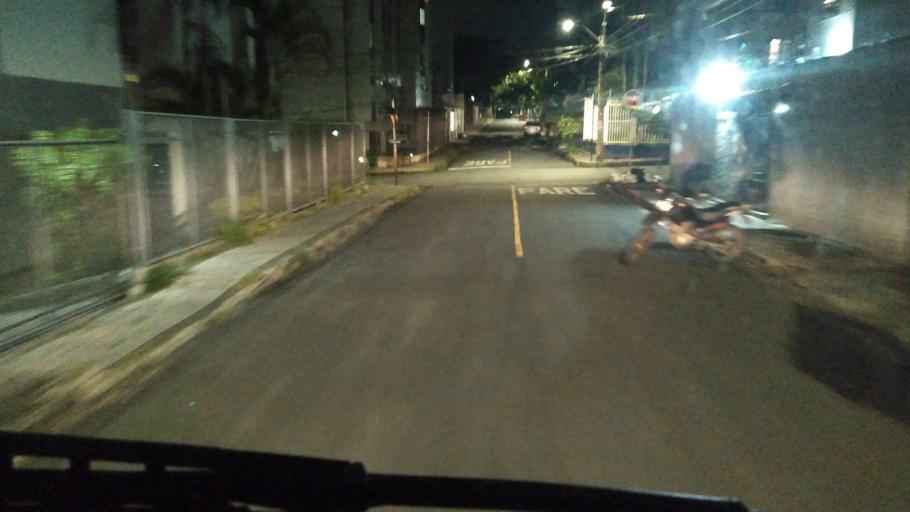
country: BR
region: Minas Gerais
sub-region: Belo Horizonte
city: Belo Horizonte
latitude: -19.9003
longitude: -43.9170
